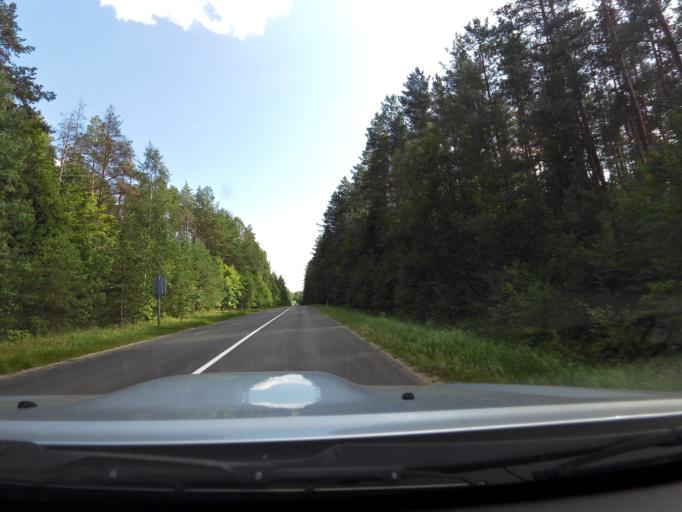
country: LT
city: Grigiskes
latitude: 54.8023
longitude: 25.0006
